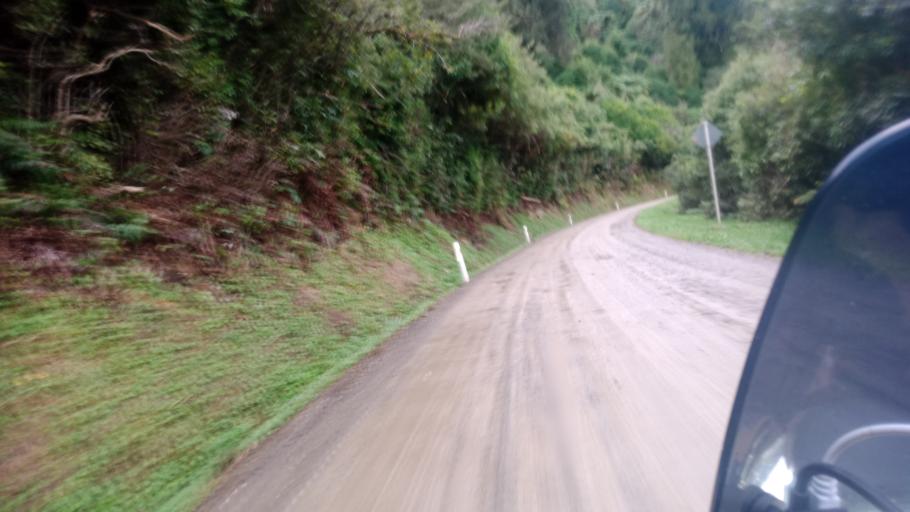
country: NZ
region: Hawke's Bay
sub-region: Wairoa District
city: Wairoa
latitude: -38.7285
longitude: 177.0912
